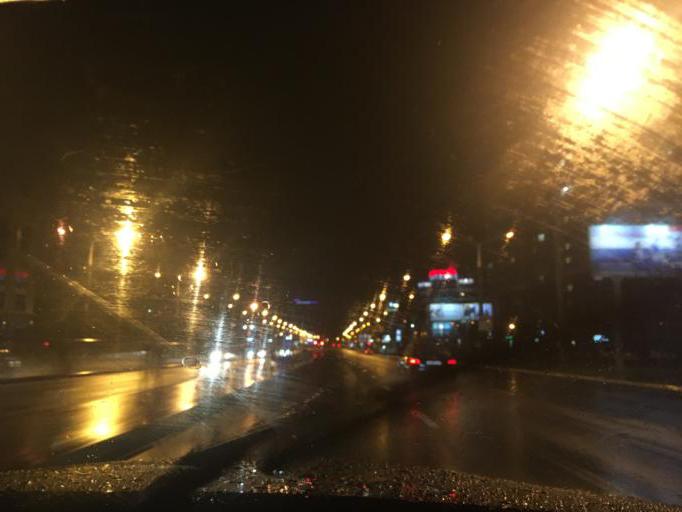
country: BY
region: Minsk
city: Minsk
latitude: 53.8893
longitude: 27.5218
